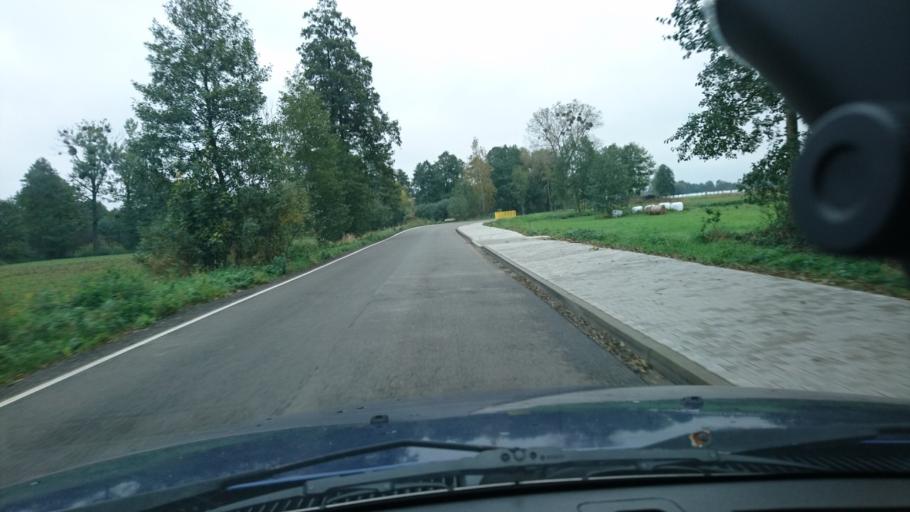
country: PL
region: Greater Poland Voivodeship
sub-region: Powiat krotoszynski
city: Sulmierzyce
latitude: 51.5711
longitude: 17.5912
